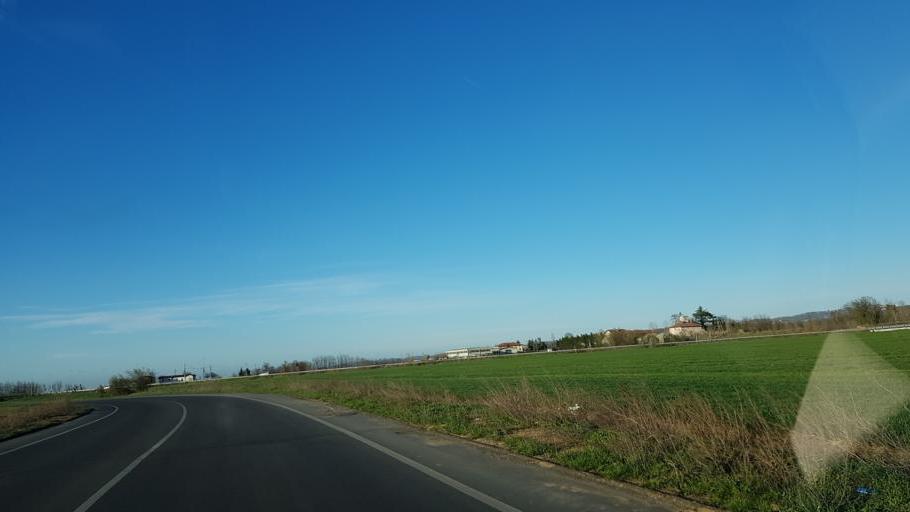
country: IT
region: Piedmont
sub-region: Provincia di Alessandria
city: Serravalle Scrivia
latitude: 44.7407
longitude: 8.8357
